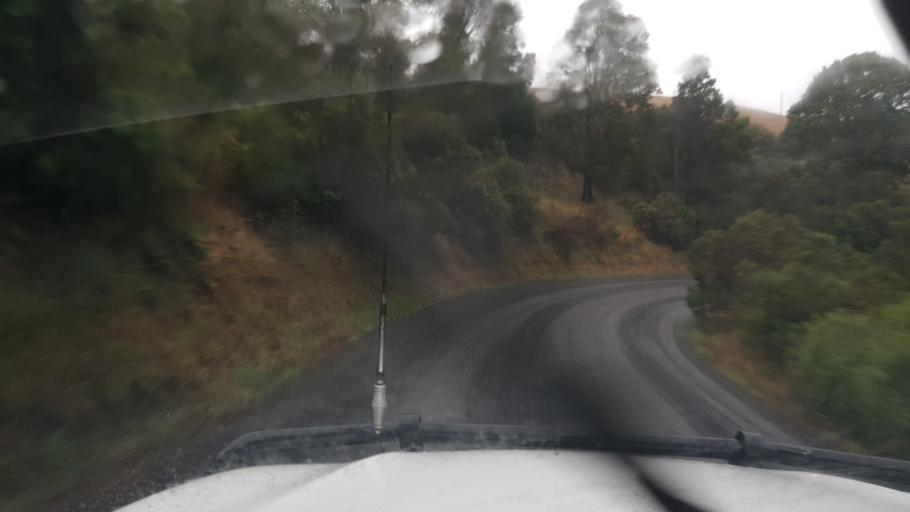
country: AU
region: Victoria
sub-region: Latrobe
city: Moe
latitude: -38.2893
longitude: 146.0972
